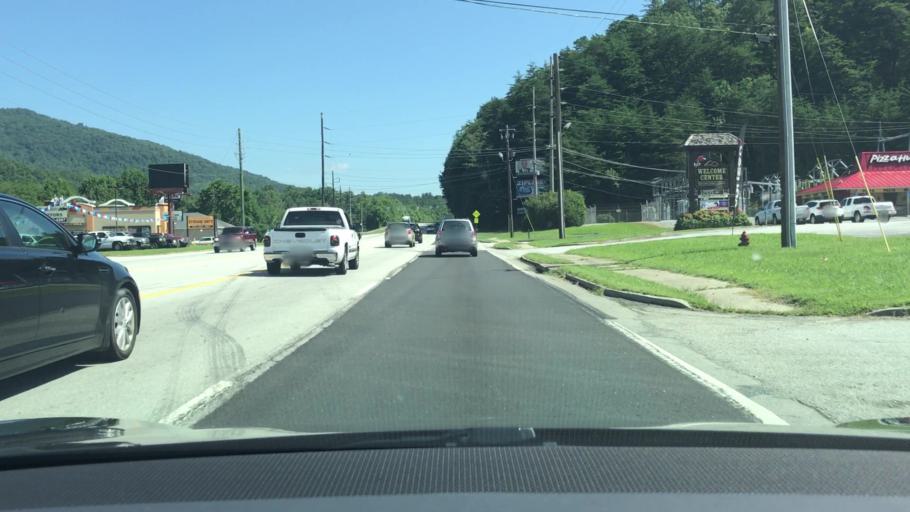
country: US
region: Georgia
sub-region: Rabun County
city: Clayton
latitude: 34.8812
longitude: -83.3963
